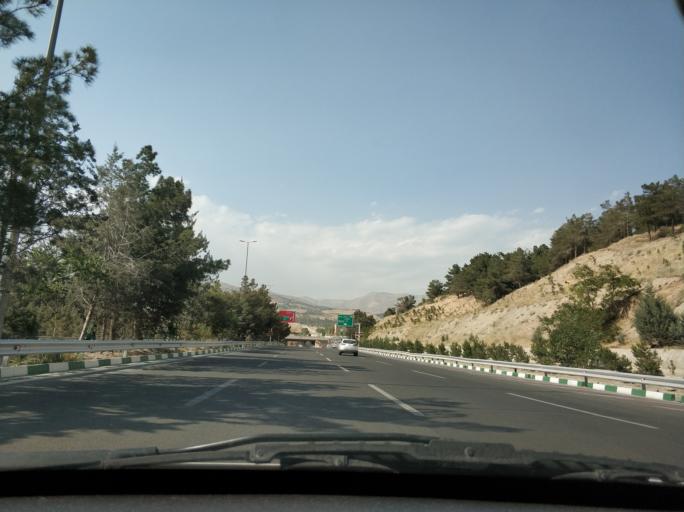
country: IR
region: Tehran
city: Tajrish
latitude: 35.7729
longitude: 51.5362
